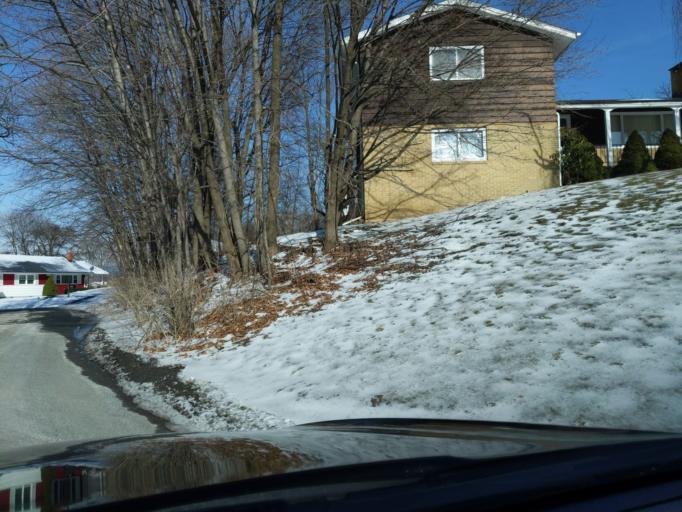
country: US
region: Pennsylvania
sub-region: Blair County
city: Greenwood
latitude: 40.5252
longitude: -78.3725
